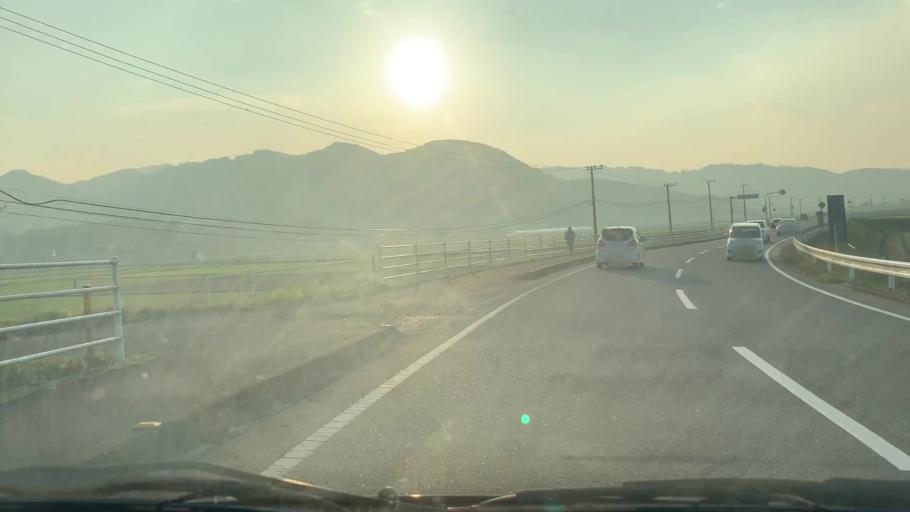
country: JP
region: Saga Prefecture
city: Takeocho-takeo
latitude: 33.2722
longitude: 130.1389
